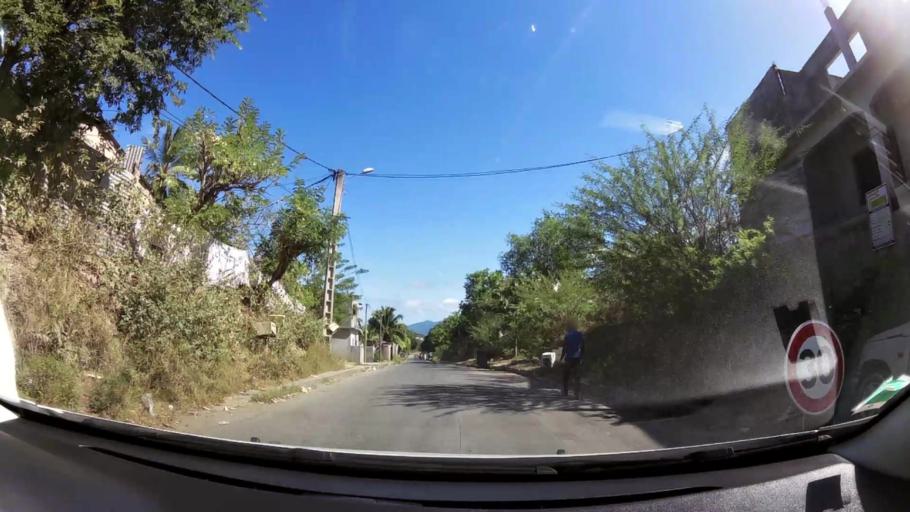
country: YT
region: Pamandzi
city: Pamandzi
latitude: -12.7826
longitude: 45.2766
